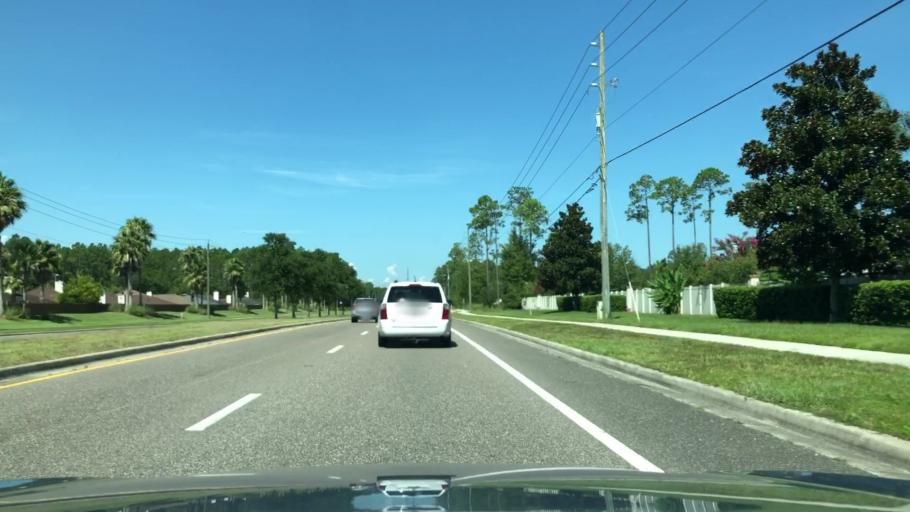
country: US
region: Florida
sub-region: Saint Johns County
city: Fruit Cove
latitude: 30.0601
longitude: -81.5177
